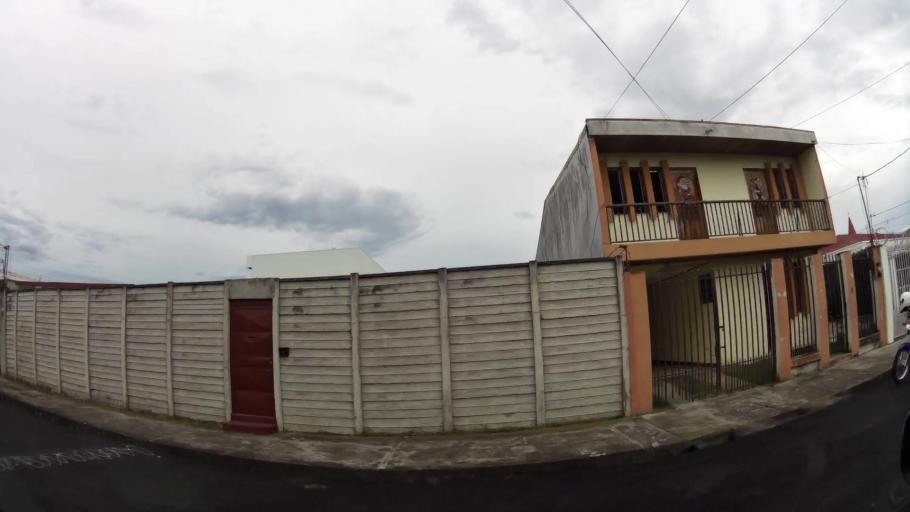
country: CR
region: San Jose
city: San Vicente de Moravia
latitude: 9.9605
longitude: -84.0502
